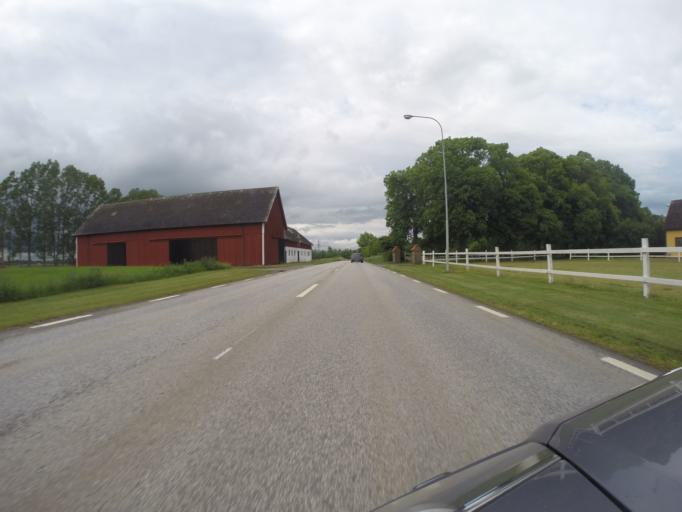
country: SE
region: Skane
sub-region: Landskrona
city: Asmundtorp
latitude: 55.8420
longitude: 12.9634
